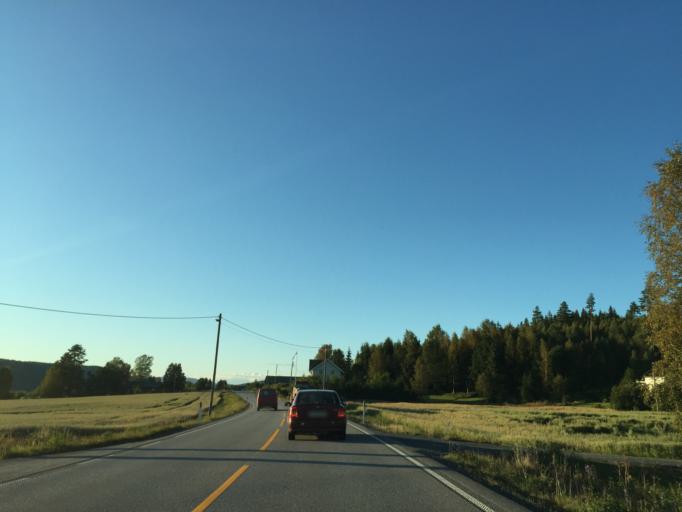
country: NO
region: Hedmark
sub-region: Nord-Odal
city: Sand
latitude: 60.4118
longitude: 11.5194
